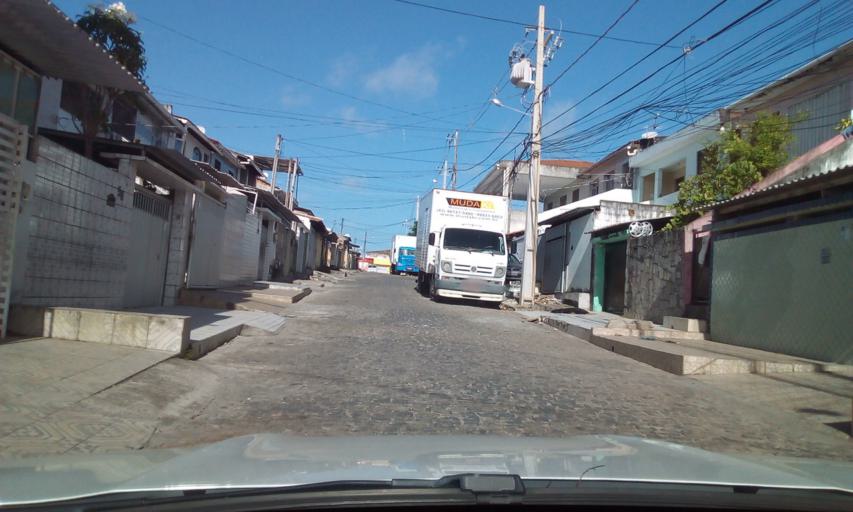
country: BR
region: Paraiba
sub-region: Joao Pessoa
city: Joao Pessoa
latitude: -7.1669
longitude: -34.8436
